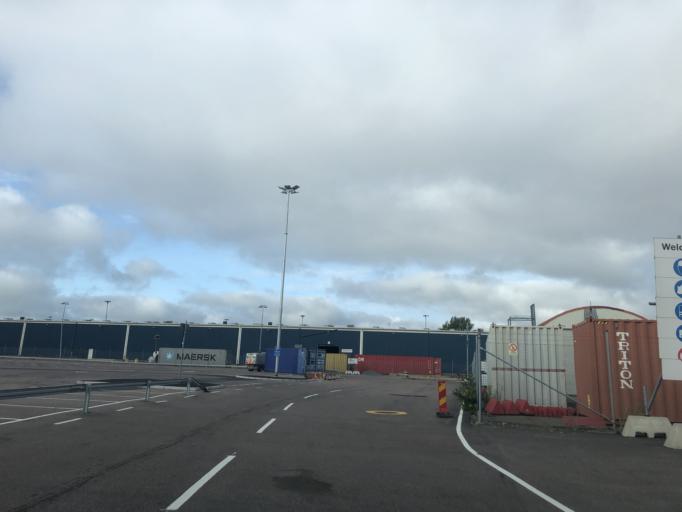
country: SE
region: Vaestra Goetaland
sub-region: Goteborg
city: Majorna
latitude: 57.6972
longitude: 11.8548
